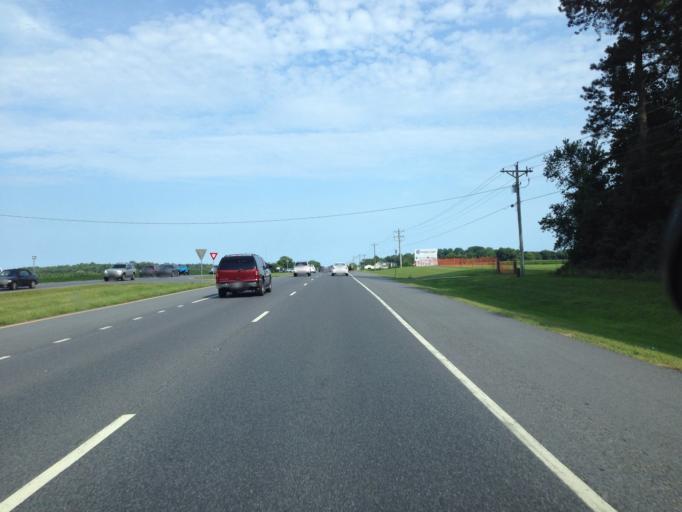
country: US
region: Delaware
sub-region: Sussex County
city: Milton
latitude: 38.8091
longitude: -75.2823
